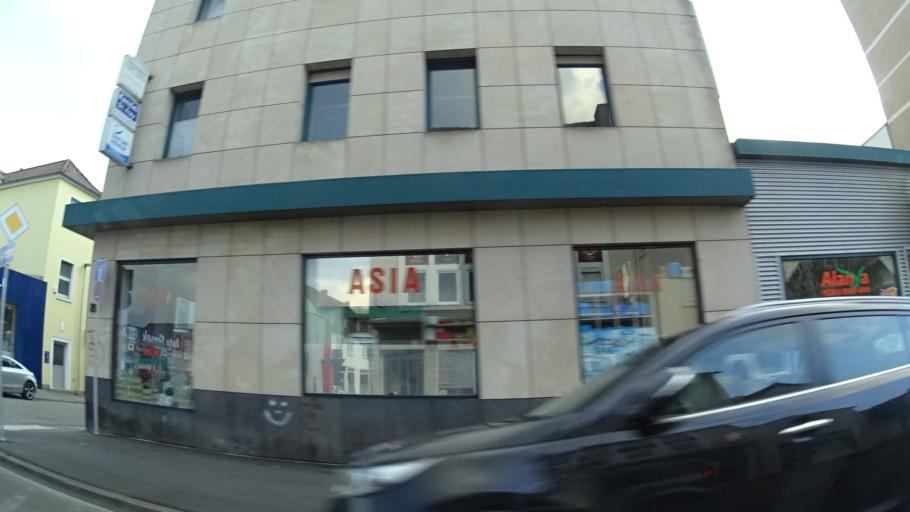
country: DE
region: Rheinland-Pfalz
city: Bad Kreuznach
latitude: 49.8396
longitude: 7.8654
